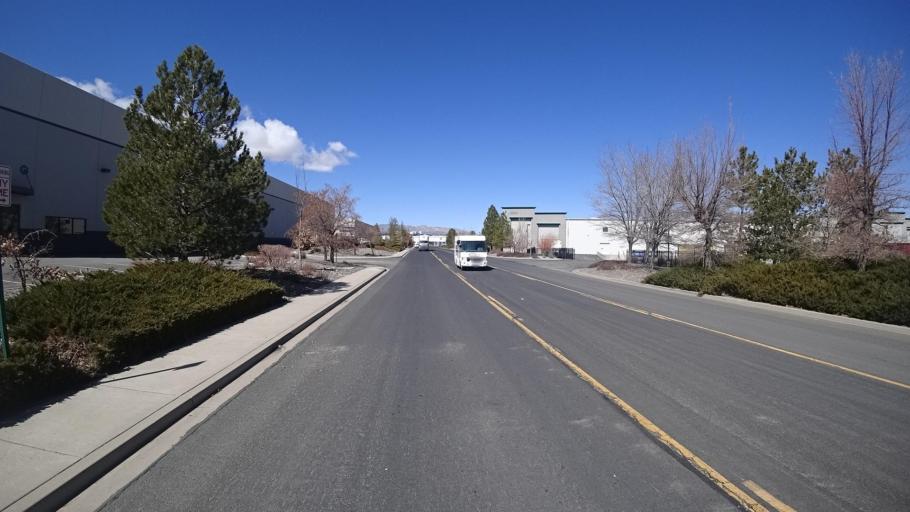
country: US
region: Nevada
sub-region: Washoe County
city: Lemmon Valley
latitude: 39.6458
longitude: -119.8612
